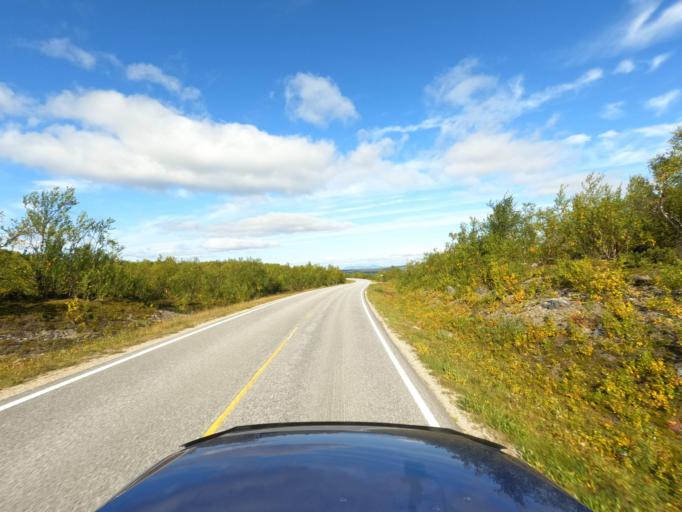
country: NO
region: Finnmark Fylke
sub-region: Karasjok
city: Karasjohka
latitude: 69.6022
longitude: 25.3272
